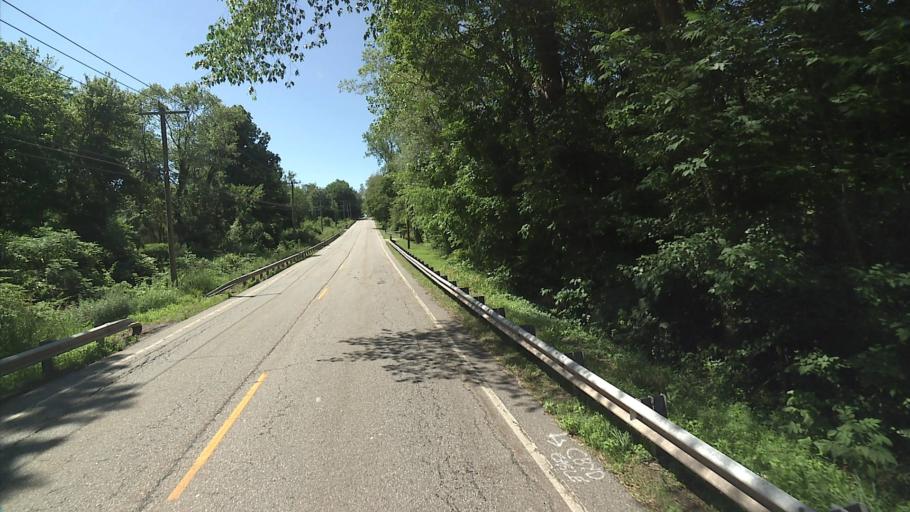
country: US
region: Connecticut
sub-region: Windham County
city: Willimantic
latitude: 41.6550
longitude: -72.2271
